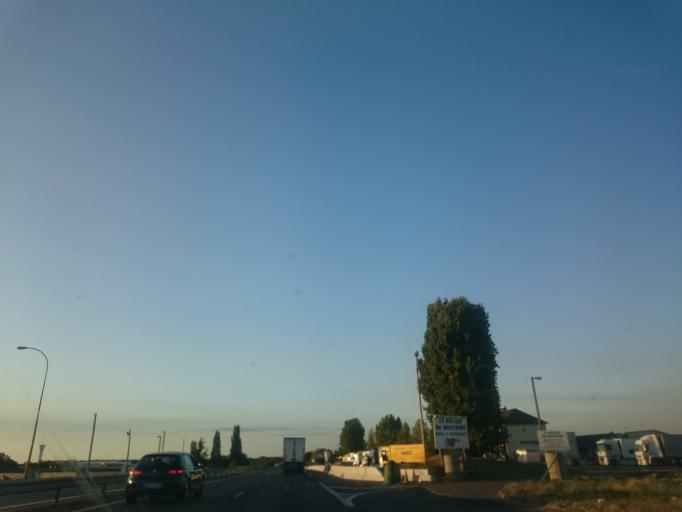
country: FR
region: Ile-de-France
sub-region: Departement de l'Essonne
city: Chamarande
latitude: 48.5223
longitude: 2.2055
